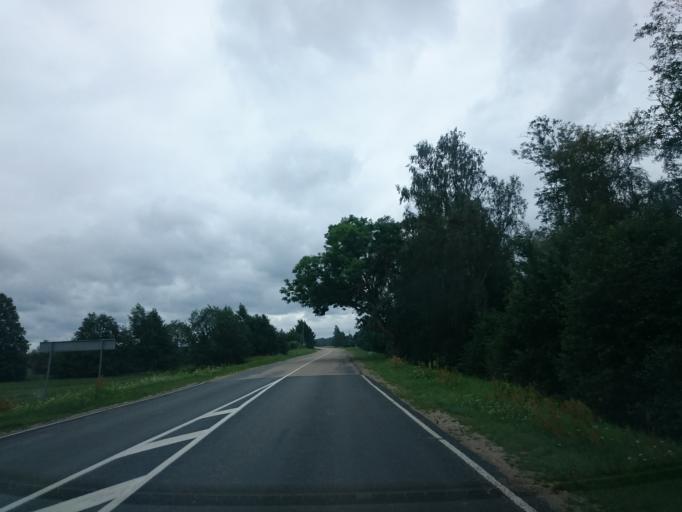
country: LV
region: Pavilostas
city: Pavilosta
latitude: 56.8783
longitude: 21.2239
